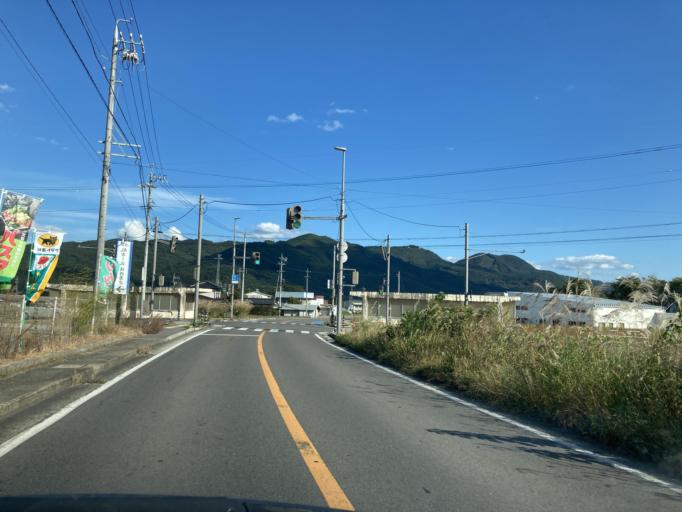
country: JP
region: Nagano
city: Omachi
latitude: 36.5225
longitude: 137.8437
